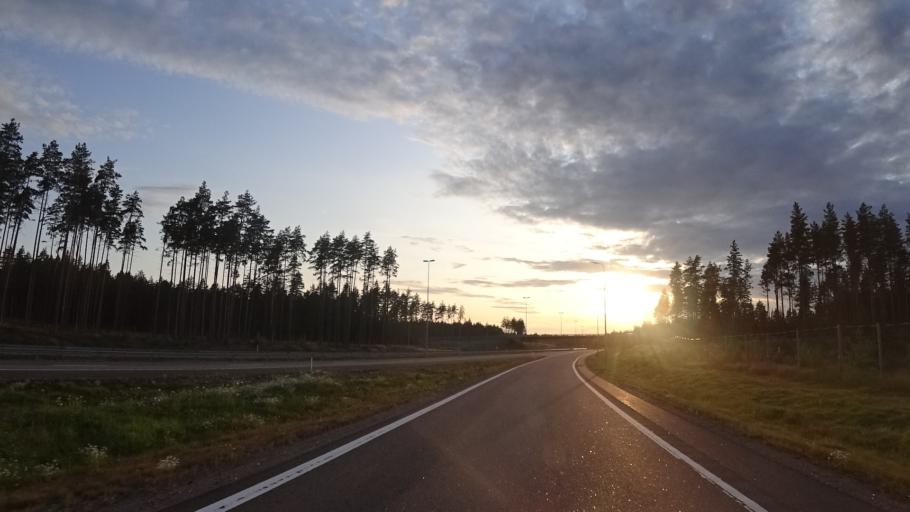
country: FI
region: Kymenlaakso
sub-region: Kotka-Hamina
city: Virojoki
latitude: 60.6115
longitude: 27.8119
